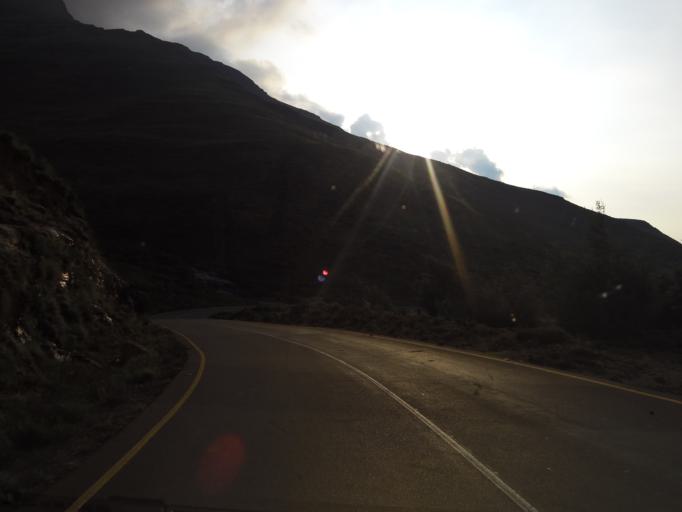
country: LS
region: Butha-Buthe
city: Butha-Buthe
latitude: -29.0599
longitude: 28.3574
